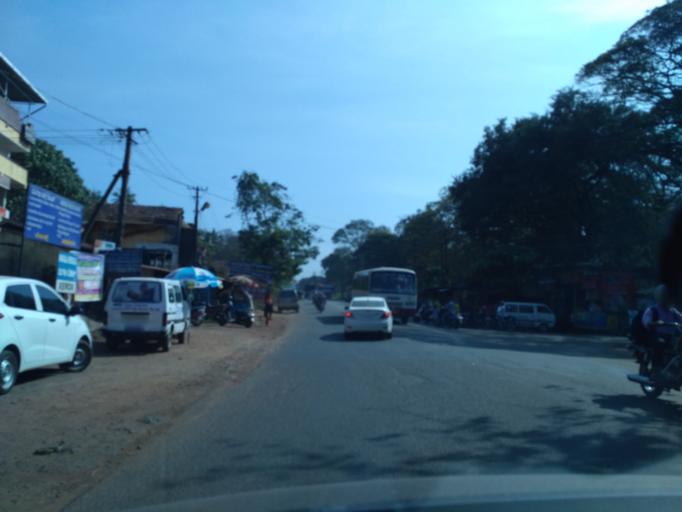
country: IN
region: Karnataka
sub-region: Dakshina Kannada
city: Mangalore
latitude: 12.8707
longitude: 74.8833
